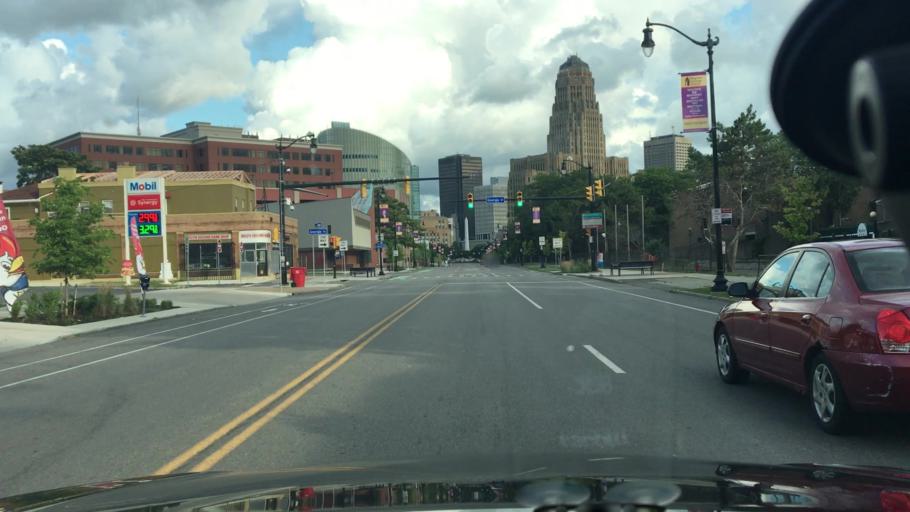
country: US
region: New York
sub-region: Erie County
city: Buffalo
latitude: 42.8907
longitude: -78.8822
